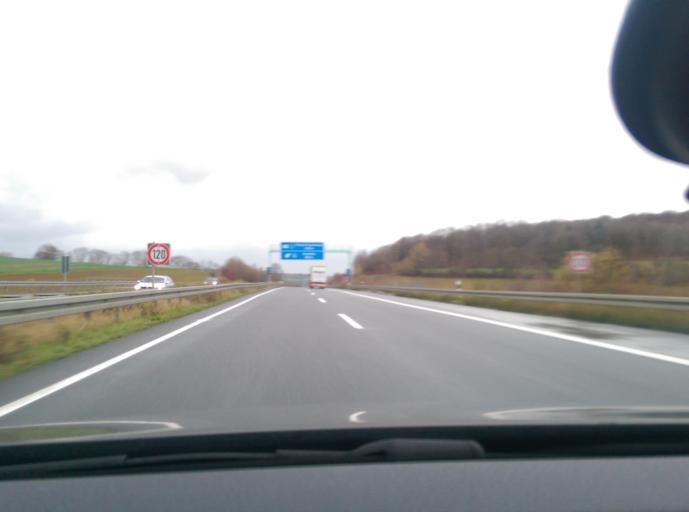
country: DE
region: Lower Saxony
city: Gemeinde Friedland
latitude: 51.4397
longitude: 9.8790
